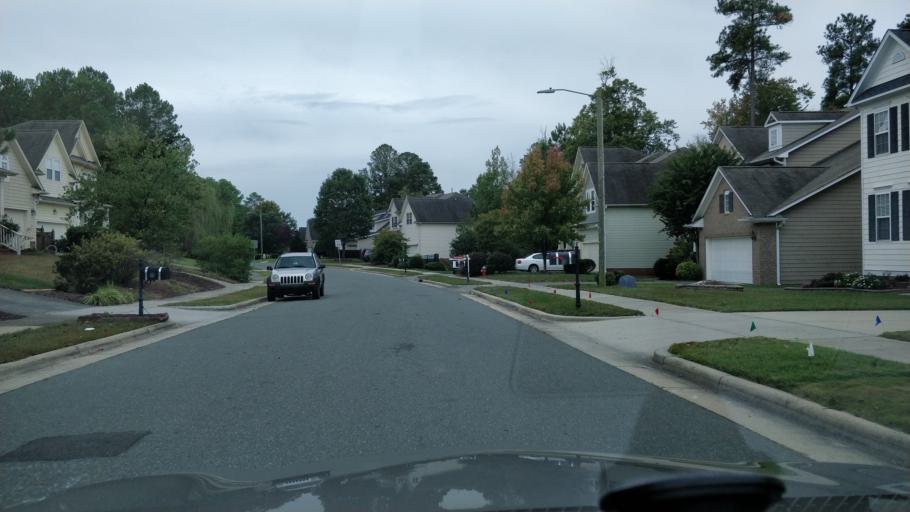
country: US
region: North Carolina
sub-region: Wake County
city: Morrisville
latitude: 35.8215
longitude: -78.8433
